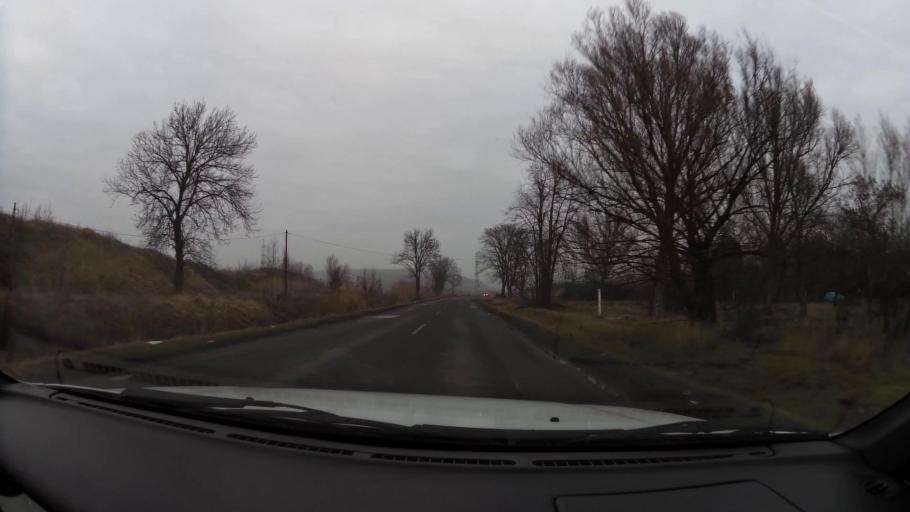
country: HU
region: Borsod-Abauj-Zemplen
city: Izsofalva
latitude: 48.2891
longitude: 20.6593
